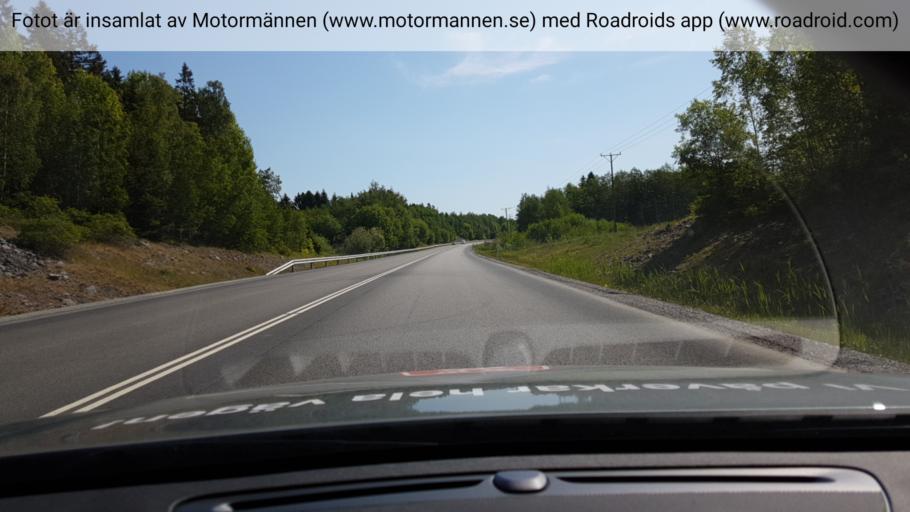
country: SE
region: Stockholm
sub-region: Norrtalje Kommun
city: Bjorko
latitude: 59.7202
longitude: 18.9441
